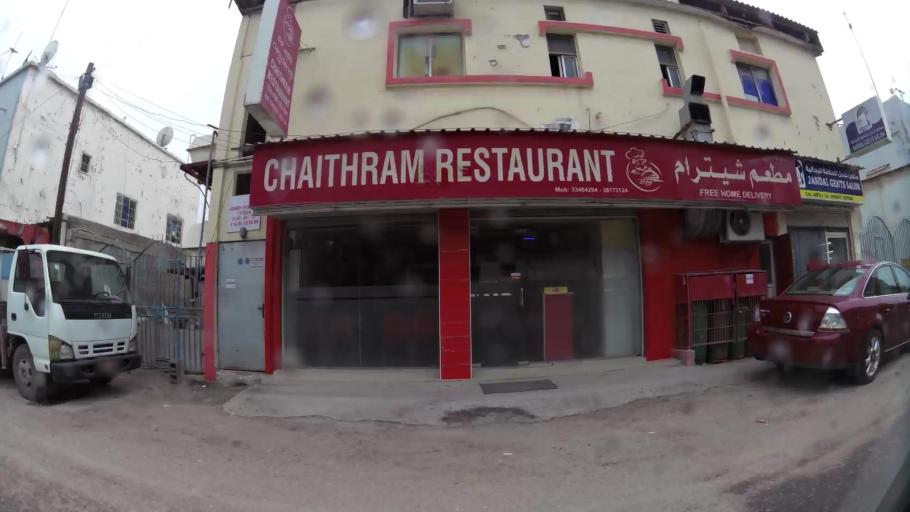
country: BH
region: Northern
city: Madinat `Isa
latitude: 26.1857
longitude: 50.5331
